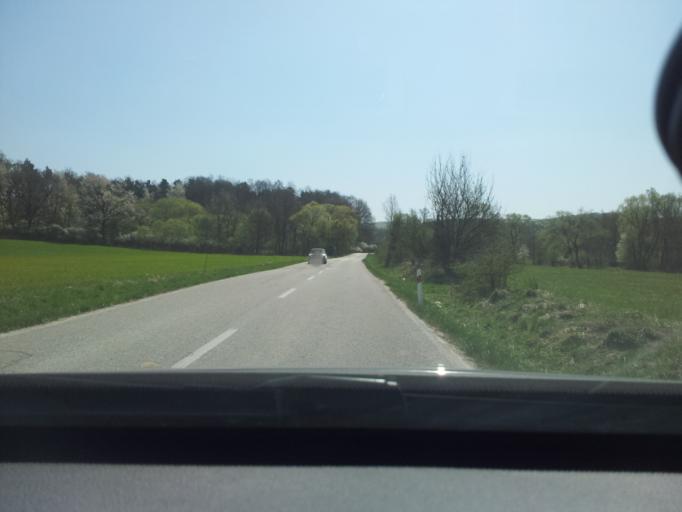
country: SK
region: Nitriansky
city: Partizanske
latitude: 48.5402
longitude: 18.3477
